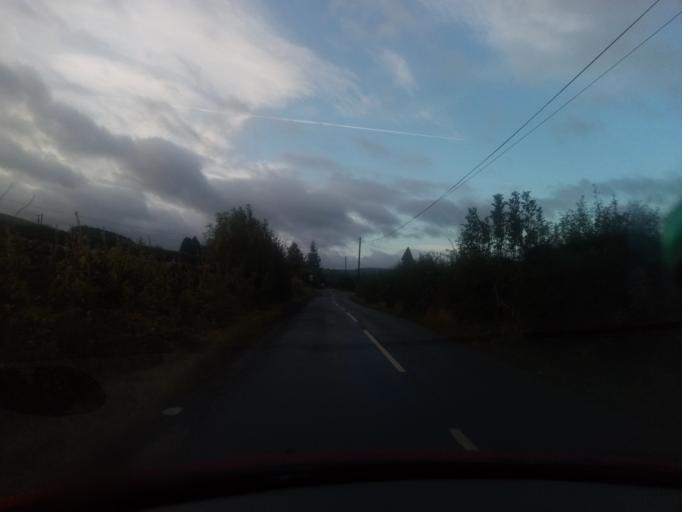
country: GB
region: Scotland
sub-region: The Scottish Borders
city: Jedburgh
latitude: 55.4143
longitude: -2.6387
